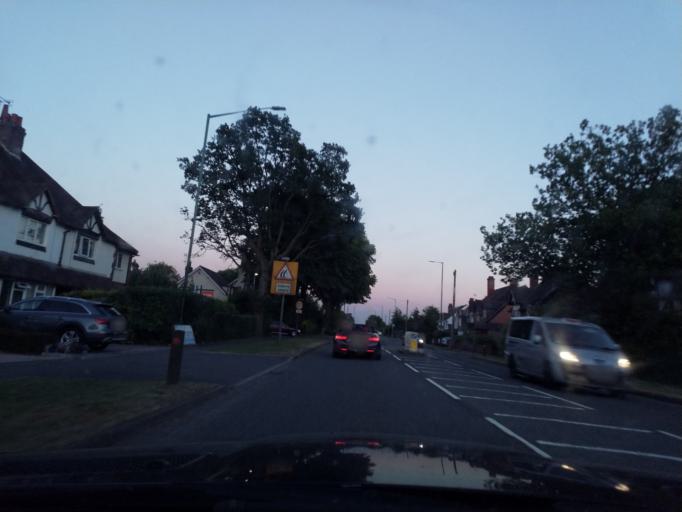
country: GB
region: England
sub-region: Solihull
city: Balsall Common
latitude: 52.3976
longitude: -1.6542
